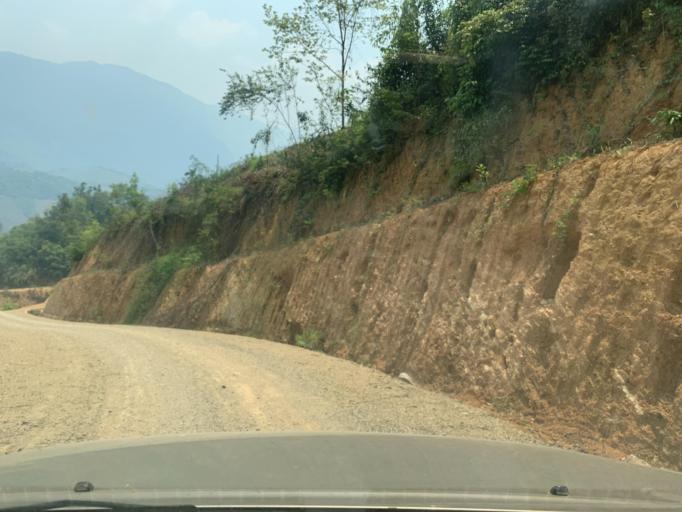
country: LA
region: Louangphabang
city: Louangphabang
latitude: 19.8604
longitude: 102.2560
